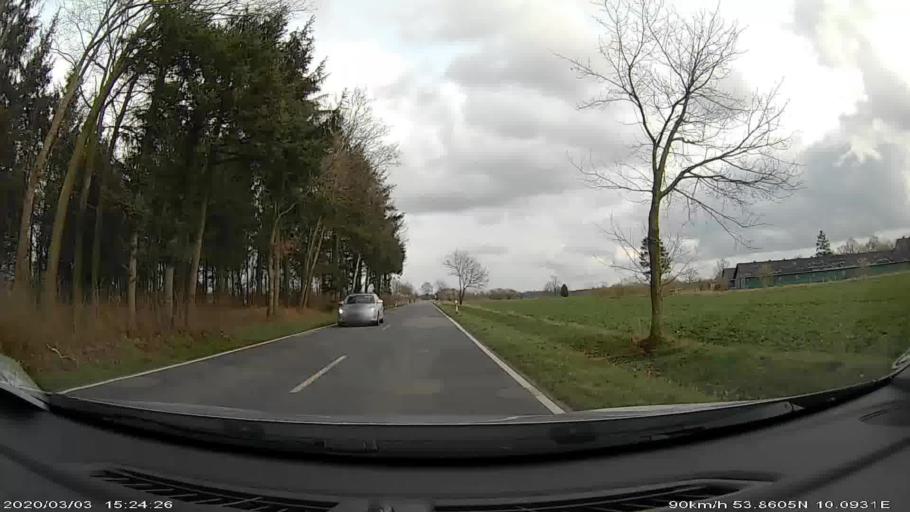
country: DE
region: Schleswig-Holstein
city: Sievershutten
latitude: 53.8602
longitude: 10.0918
